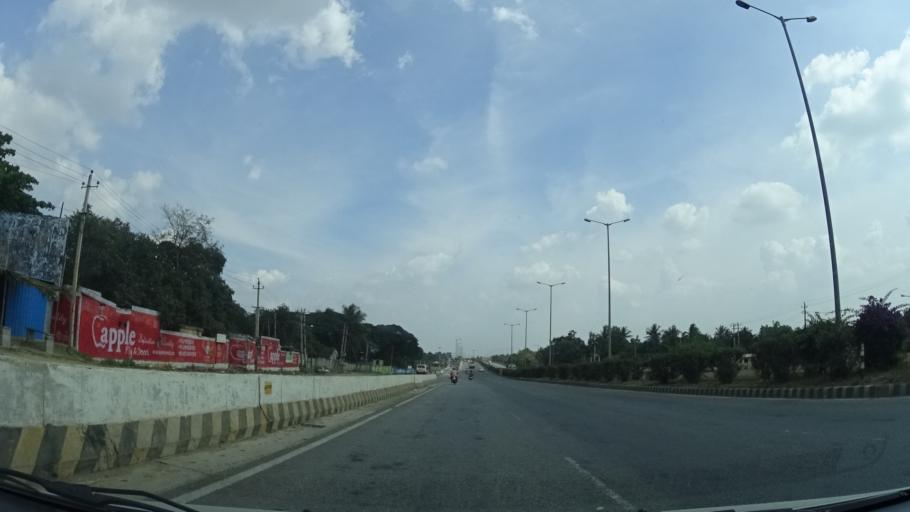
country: IN
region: Karnataka
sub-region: Bangalore Rural
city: Nelamangala
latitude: 13.0843
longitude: 77.4149
